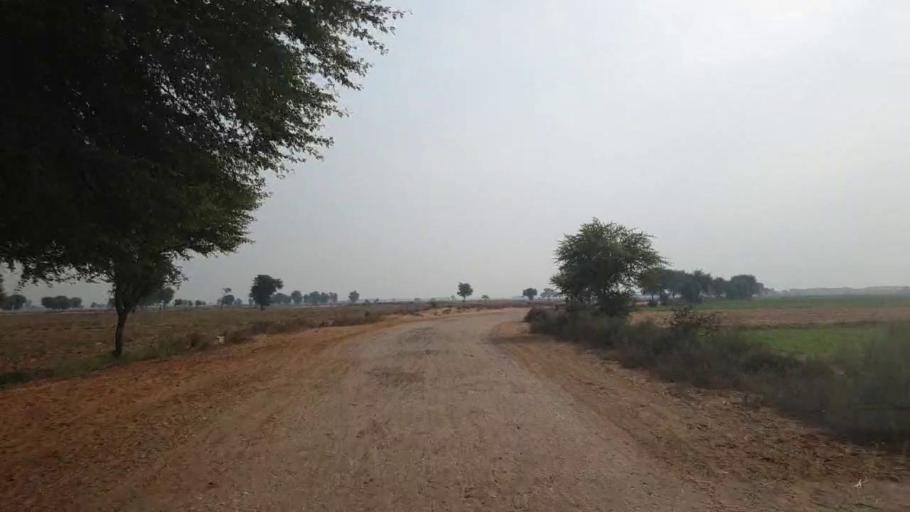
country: PK
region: Sindh
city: Sann
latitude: 26.0247
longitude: 68.1425
